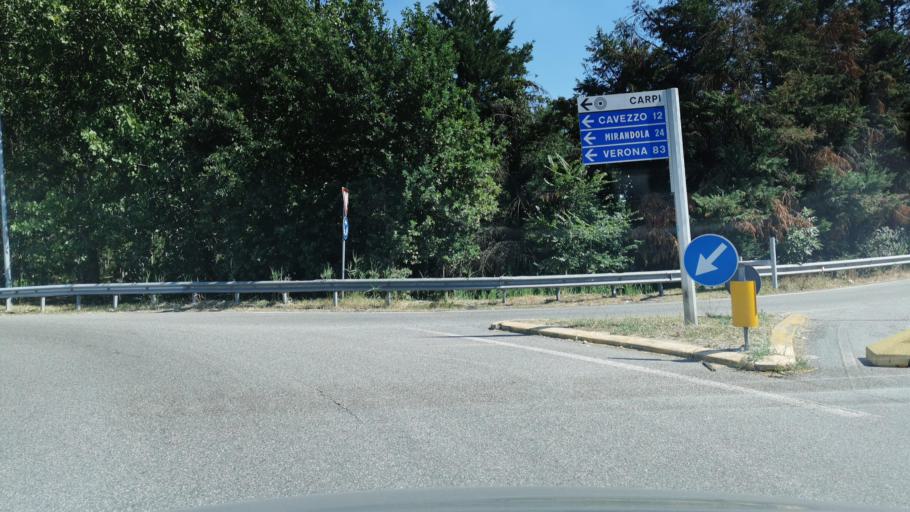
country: IT
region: Emilia-Romagna
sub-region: Provincia di Modena
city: Fossoli
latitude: 44.8049
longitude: 10.8943
